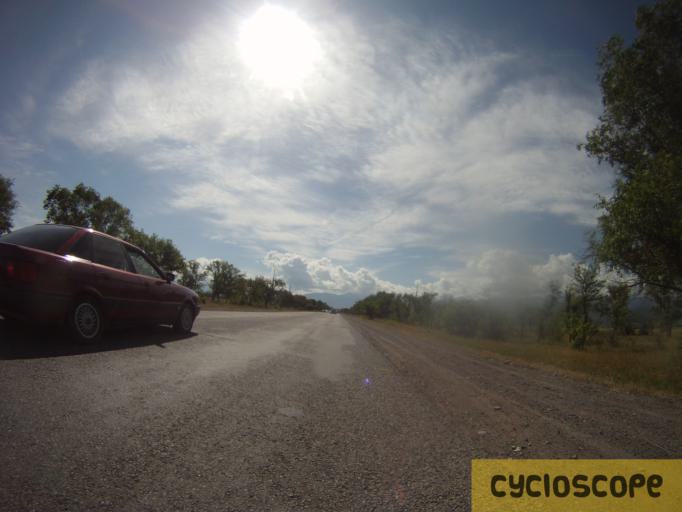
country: KZ
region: Almaty Oblysy
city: Esik
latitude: 43.3987
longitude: 77.3858
